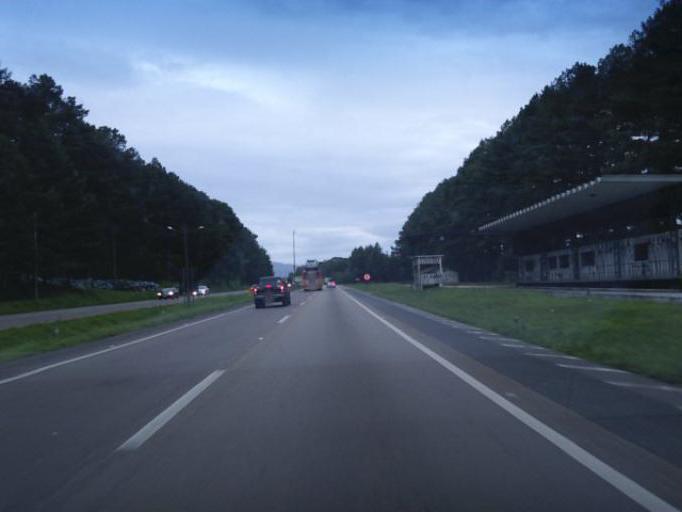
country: BR
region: Parana
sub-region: Sao Jose Dos Pinhais
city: Sao Jose dos Pinhais
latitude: -25.8273
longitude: -49.1203
